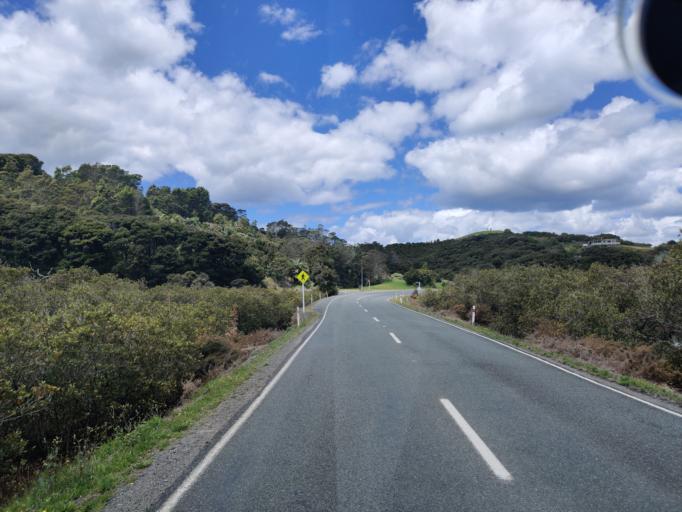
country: NZ
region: Northland
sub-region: Far North District
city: Paihia
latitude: -35.2733
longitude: 174.1387
